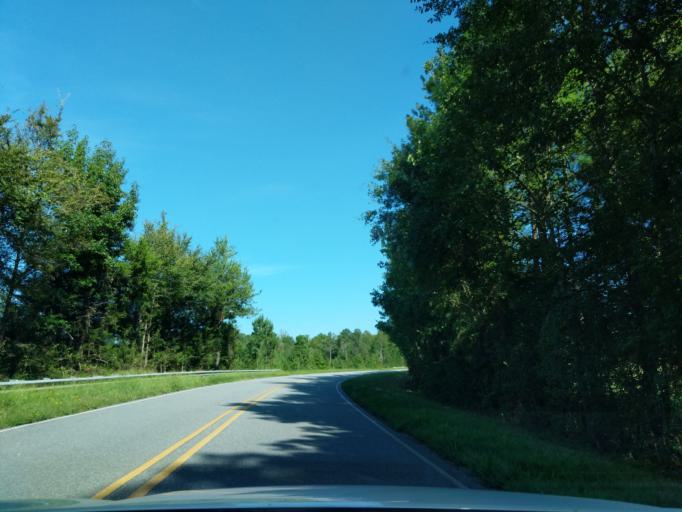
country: US
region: Georgia
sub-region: Madison County
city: Comer
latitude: 33.9748
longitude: -83.0834
